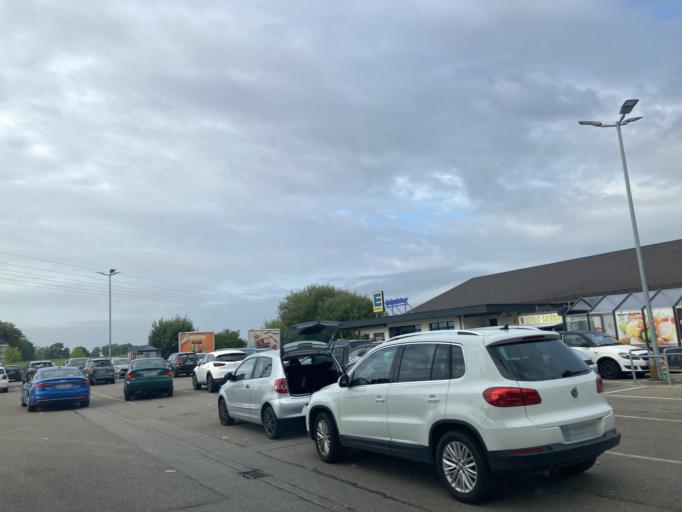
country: DE
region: Bavaria
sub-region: Swabia
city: Oettingen in Bayern
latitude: 48.9453
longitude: 10.5946
